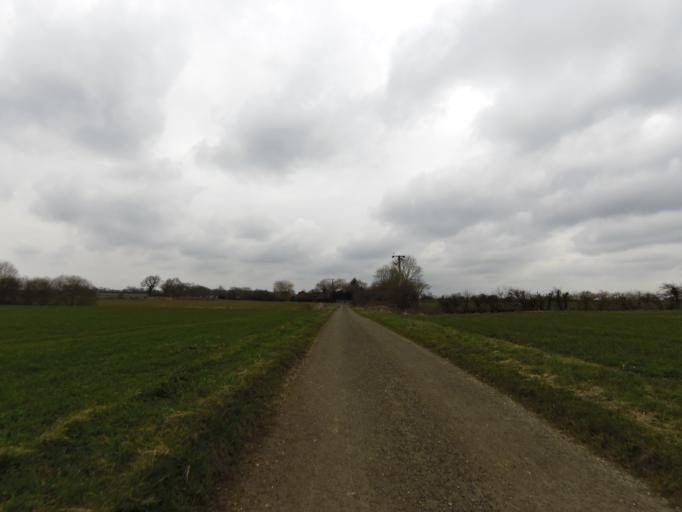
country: GB
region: England
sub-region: Suffolk
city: Halesworth
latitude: 52.3708
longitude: 1.5180
